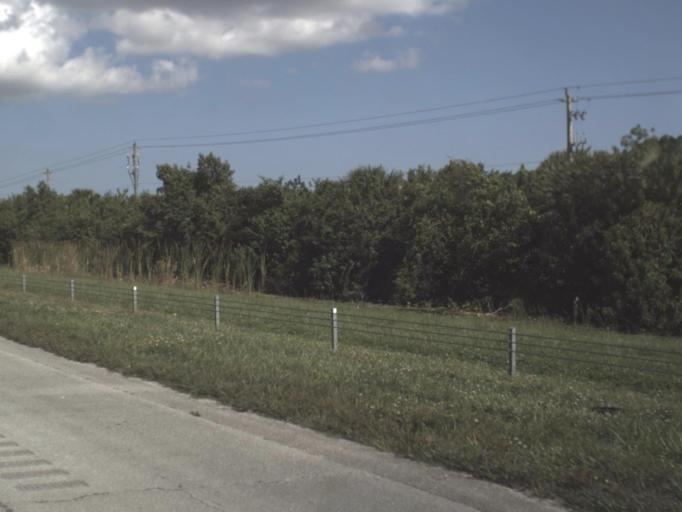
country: US
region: Florida
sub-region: Palm Beach County
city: Palm Beach Gardens
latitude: 26.8243
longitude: -80.1305
